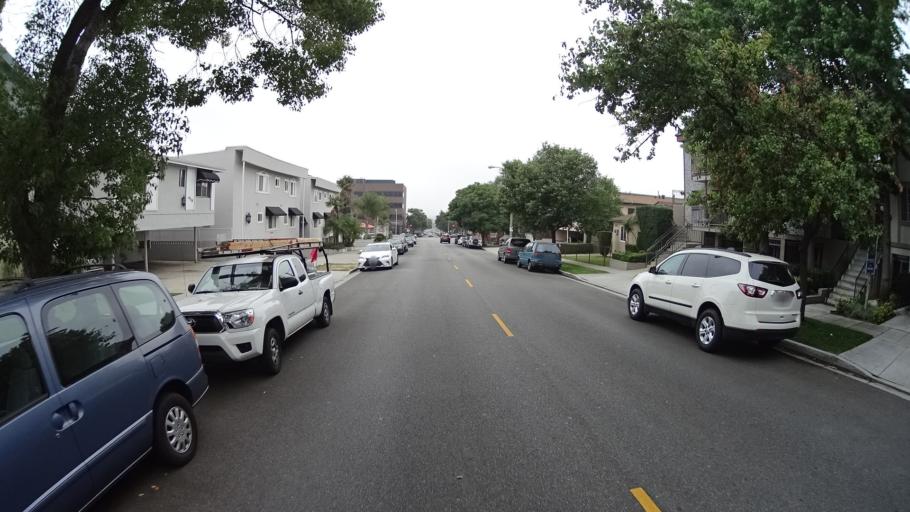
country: US
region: California
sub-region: Los Angeles County
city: Burbank
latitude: 34.1804
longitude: -118.3005
